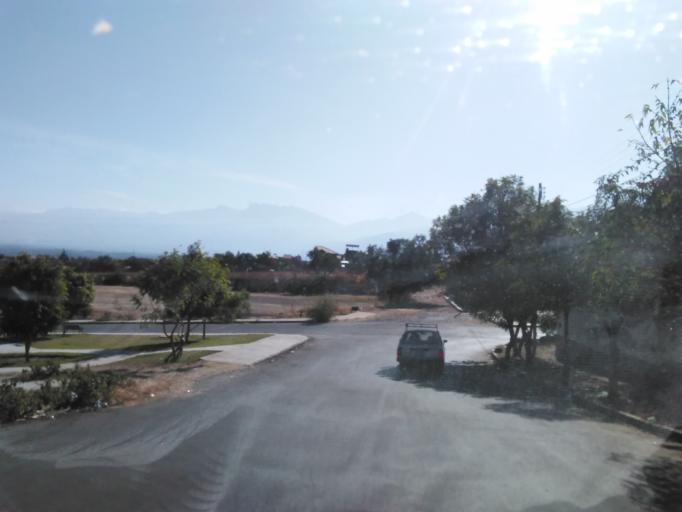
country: BO
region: Cochabamba
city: Cochabamba
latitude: -17.3546
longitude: -66.1647
